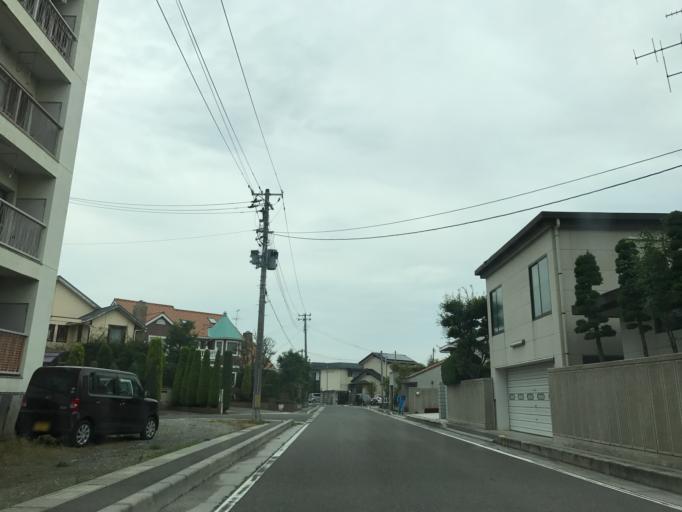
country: JP
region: Fukushima
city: Koriyama
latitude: 37.4101
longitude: 140.3650
